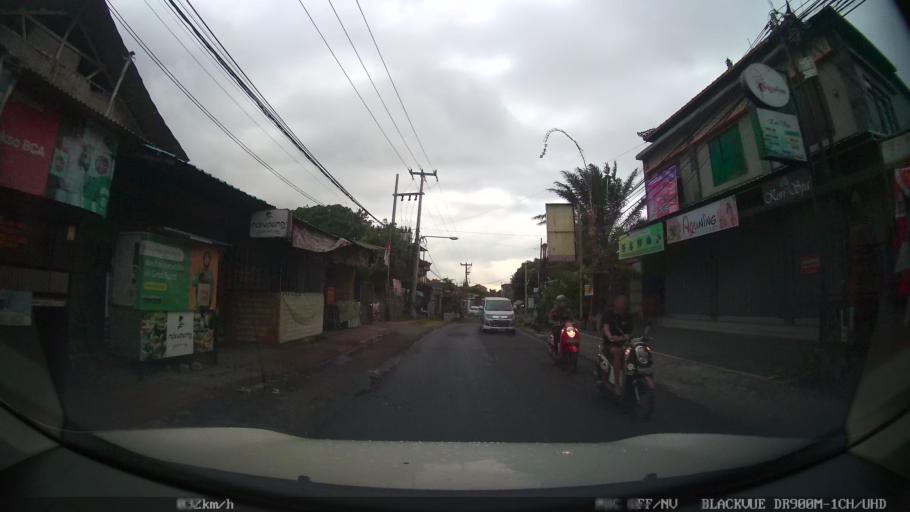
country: ID
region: Bali
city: Banjar Kertajiwa
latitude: -8.6280
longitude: 115.2617
